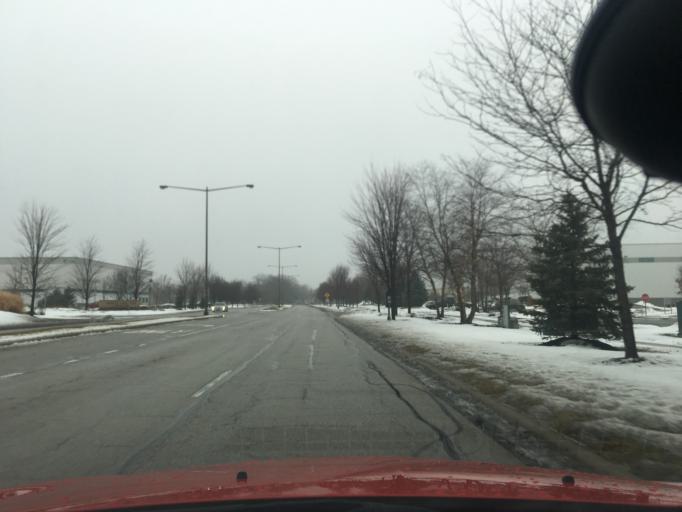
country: US
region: Illinois
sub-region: Kane County
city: North Aurora
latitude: 41.7948
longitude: -88.2654
